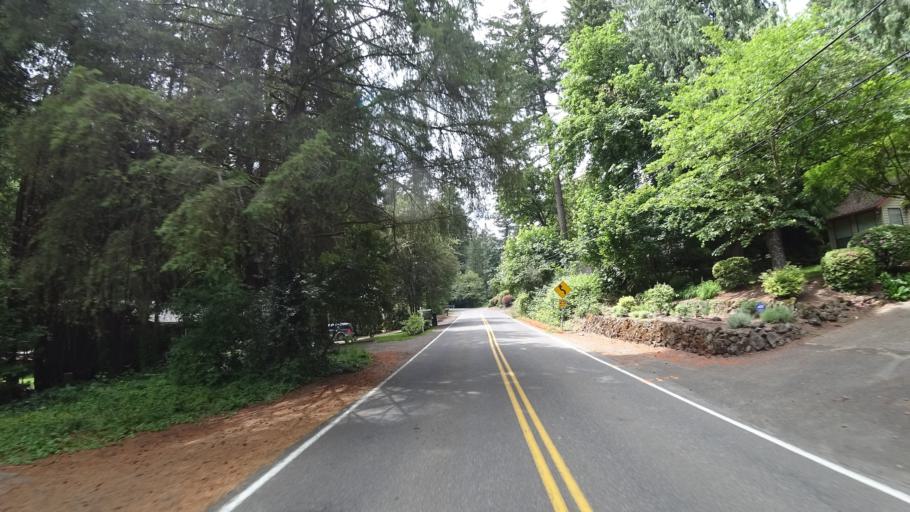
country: US
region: Oregon
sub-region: Clackamas County
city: Lake Oswego
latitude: 45.4452
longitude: -122.7087
